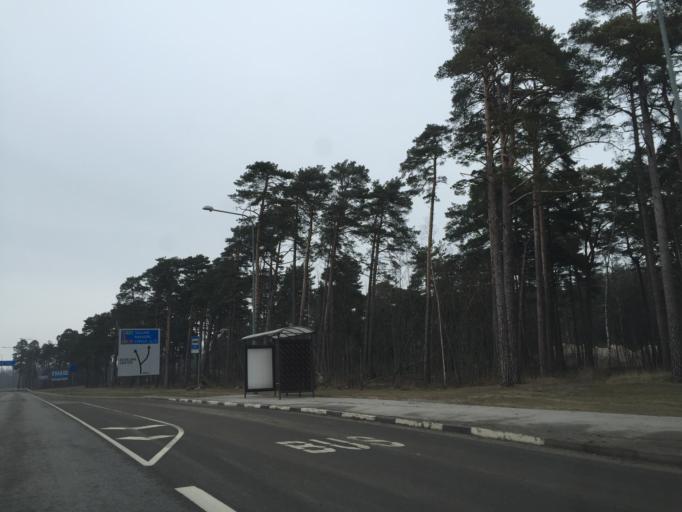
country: EE
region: Paernumaa
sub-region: Paikuse vald
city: Paikuse
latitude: 58.3576
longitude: 24.5742
